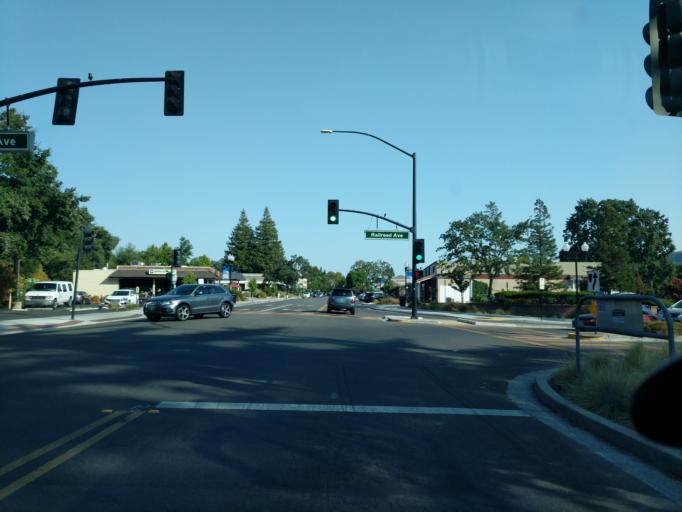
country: US
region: California
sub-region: Contra Costa County
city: Danville
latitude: 37.8249
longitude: -122.0034
